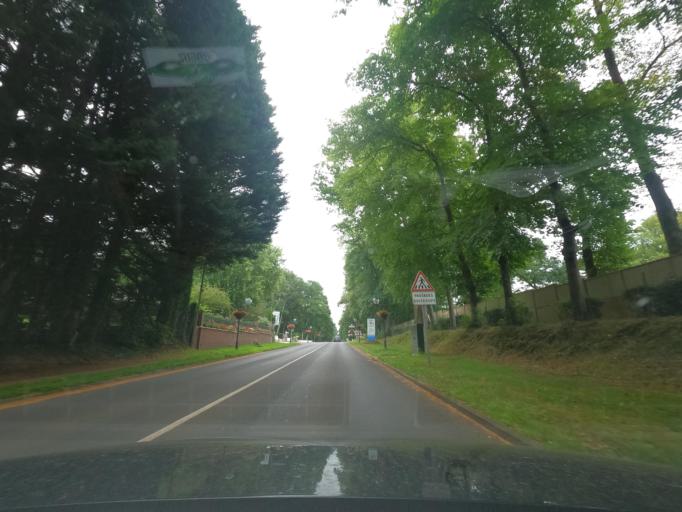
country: FR
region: Haute-Normandie
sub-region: Departement de la Seine-Maritime
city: Forges-les-Eaux
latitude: 49.6084
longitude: 1.5257
